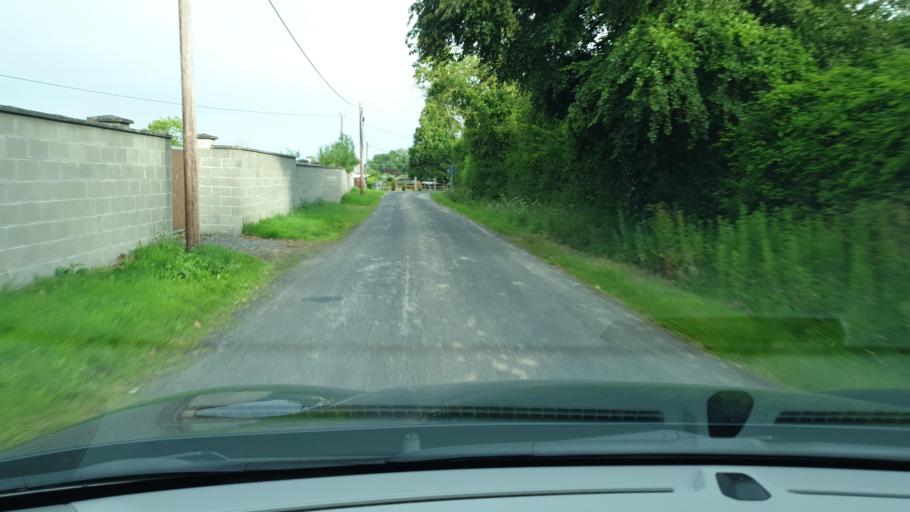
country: IE
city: Confey
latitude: 53.4085
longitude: -6.5118
